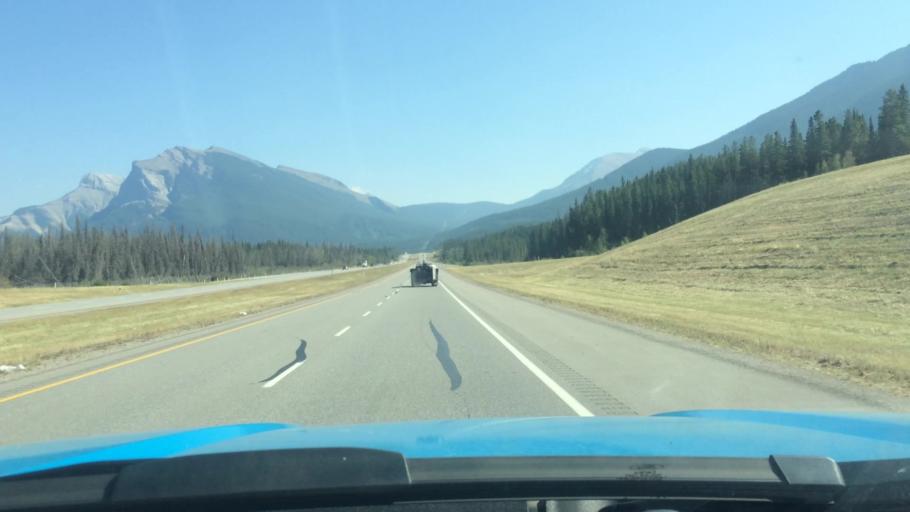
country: CA
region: Alberta
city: Canmore
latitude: 51.0551
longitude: -115.3135
